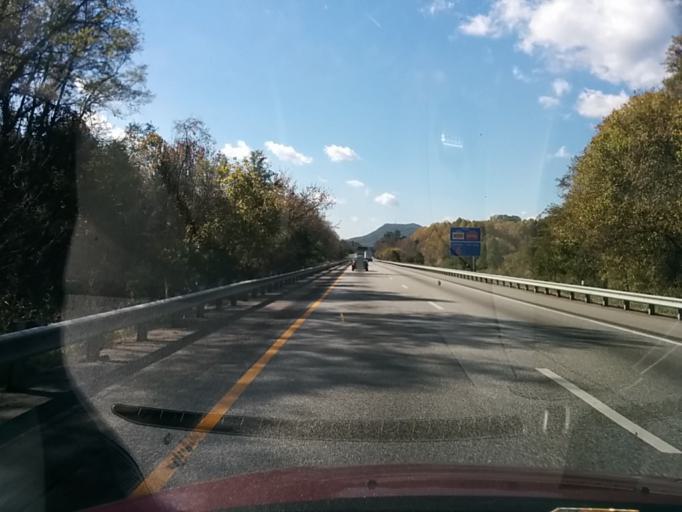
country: US
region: Virginia
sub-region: Botetourt County
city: Daleville
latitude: 37.4180
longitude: -79.8845
